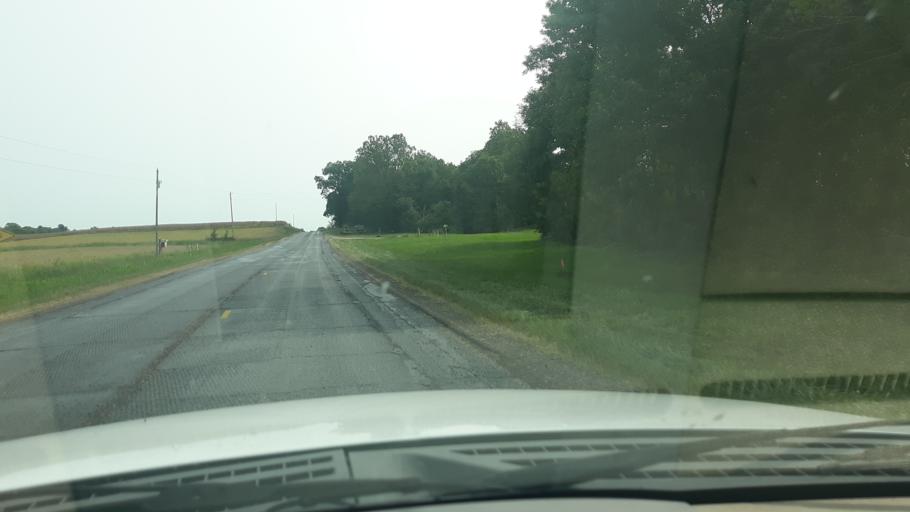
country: US
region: Illinois
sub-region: Edwards County
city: Grayville
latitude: 38.2941
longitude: -87.9673
